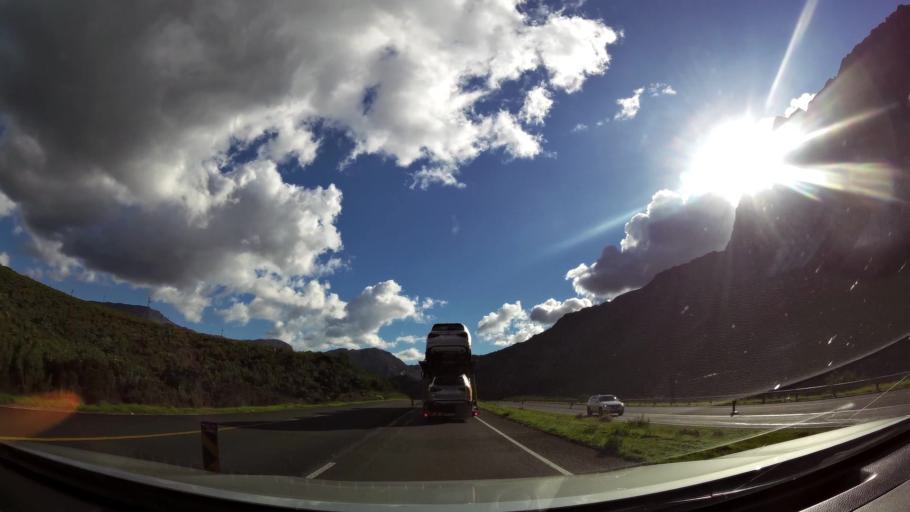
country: ZA
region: Western Cape
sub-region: Cape Winelands District Municipality
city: Paarl
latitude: -33.7247
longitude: 19.1495
